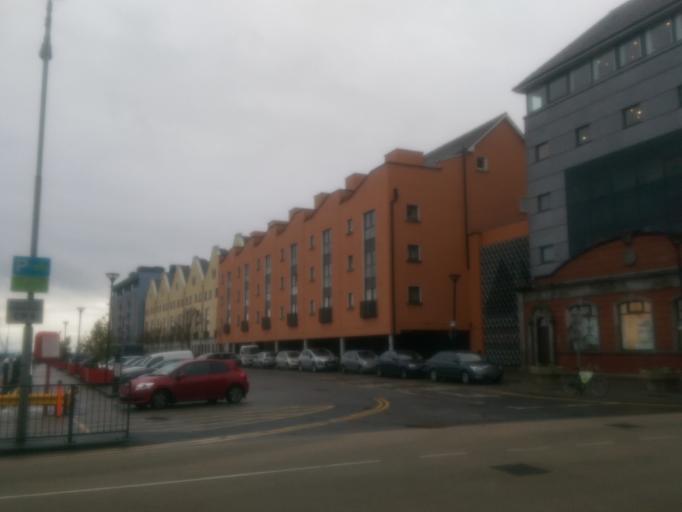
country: IE
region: Connaught
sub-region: County Galway
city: Gaillimh
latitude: 53.2700
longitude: -9.0520
